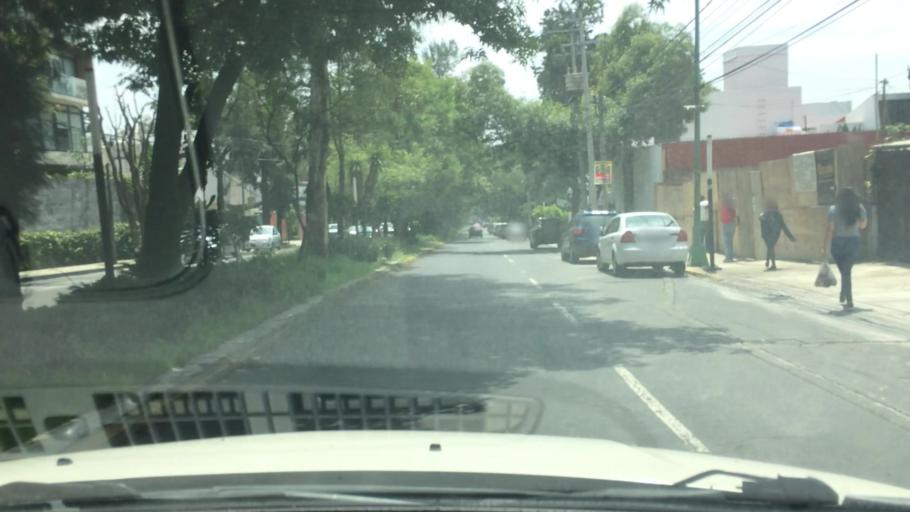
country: MX
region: Mexico City
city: Alvaro Obregon
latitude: 19.3581
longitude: -99.2052
